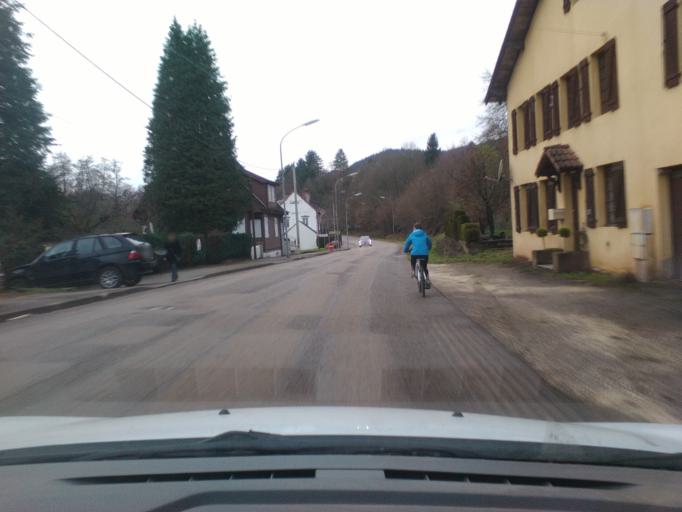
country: FR
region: Lorraine
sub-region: Departement des Vosges
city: Senones
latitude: 48.3933
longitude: 6.9684
